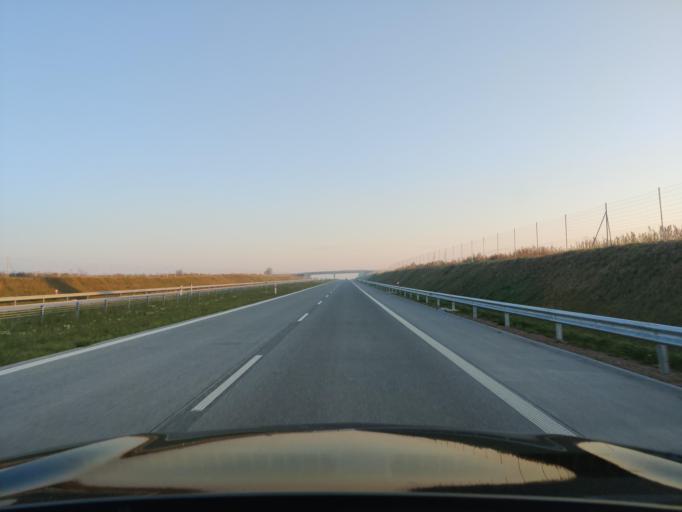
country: PL
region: Masovian Voivodeship
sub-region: Powiat mlawski
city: Wisniewo
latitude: 53.0566
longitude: 20.3641
